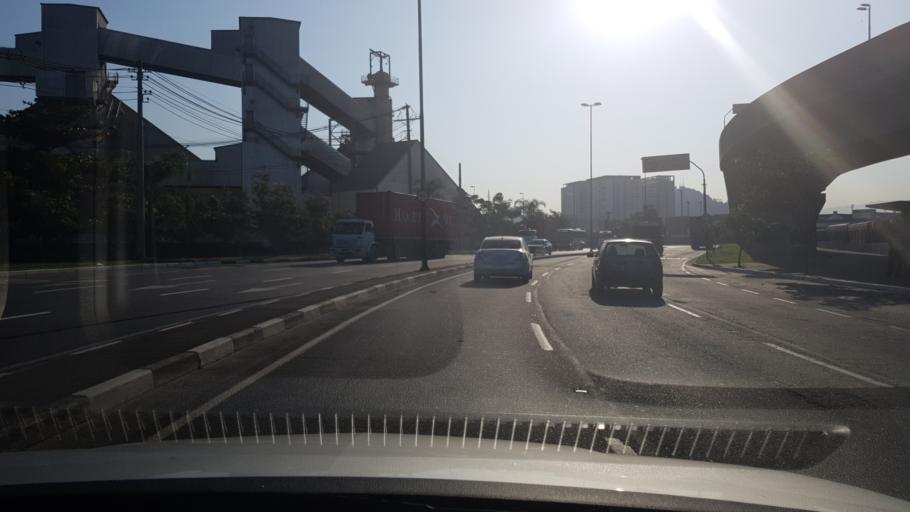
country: BR
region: Sao Paulo
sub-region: Santos
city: Santos
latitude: -23.9517
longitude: -46.3132
